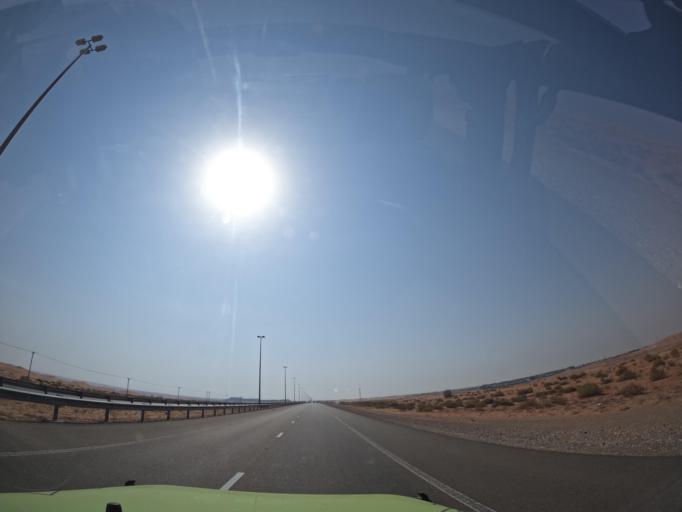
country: OM
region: Al Buraimi
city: Al Buraymi
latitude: 24.4268
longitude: 55.6821
